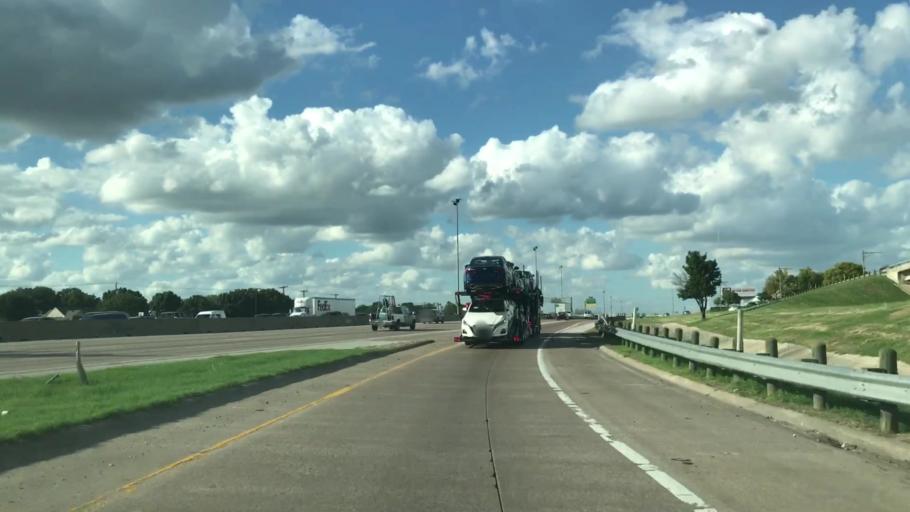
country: US
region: Texas
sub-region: Dallas County
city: Mesquite
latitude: 32.8252
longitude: -96.6299
